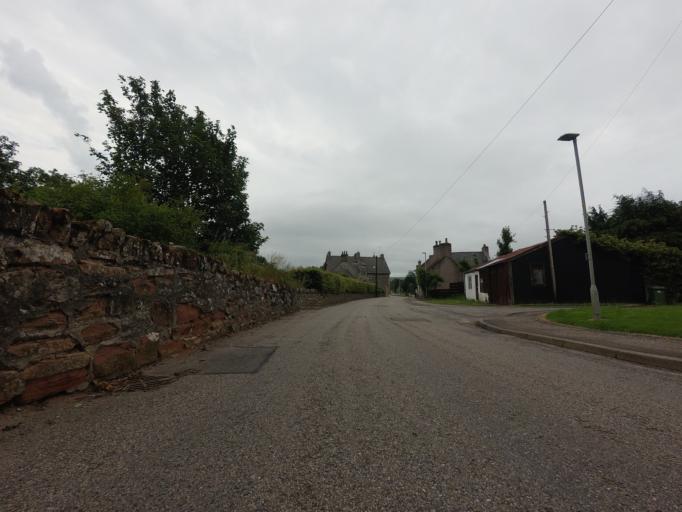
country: GB
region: Scotland
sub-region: Highland
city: Alness
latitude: 57.8827
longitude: -4.3638
